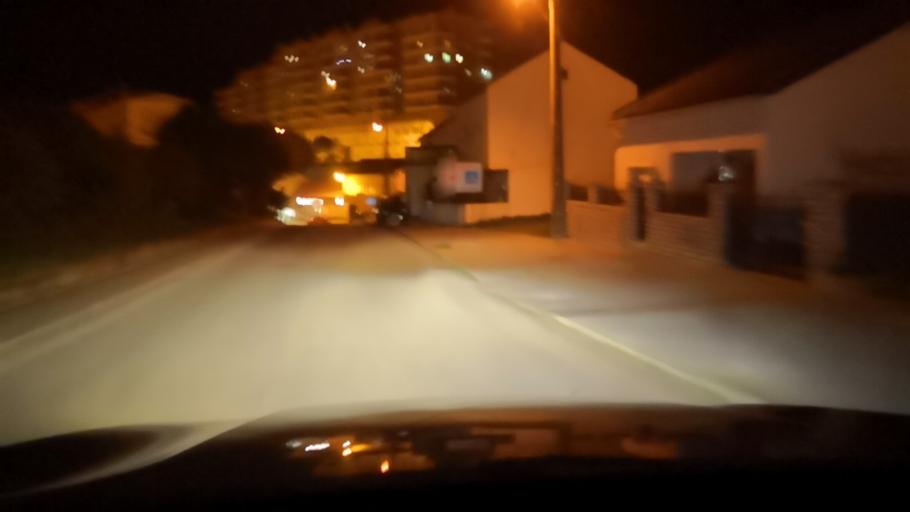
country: PT
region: Setubal
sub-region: Setubal
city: Setubal
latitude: 38.5268
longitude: -8.9082
